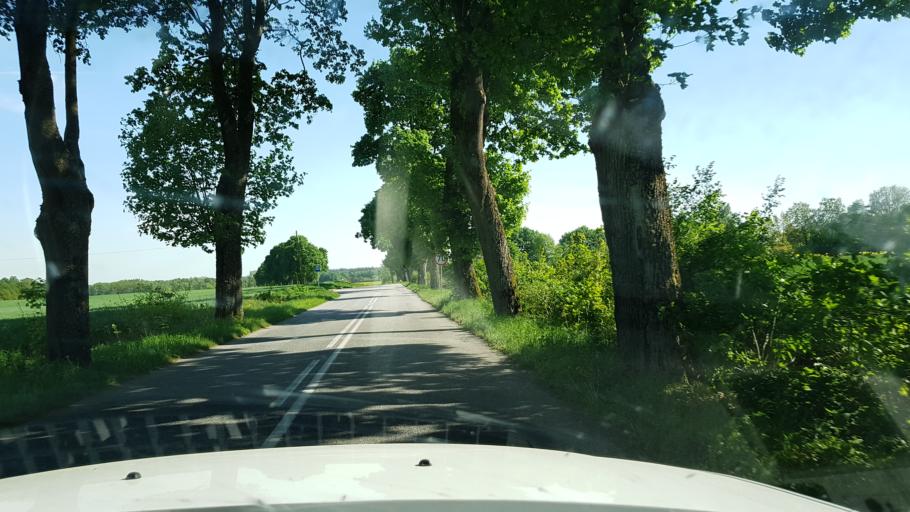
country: PL
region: West Pomeranian Voivodeship
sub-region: Powiat lobeski
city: Resko
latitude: 53.8312
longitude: 15.3879
